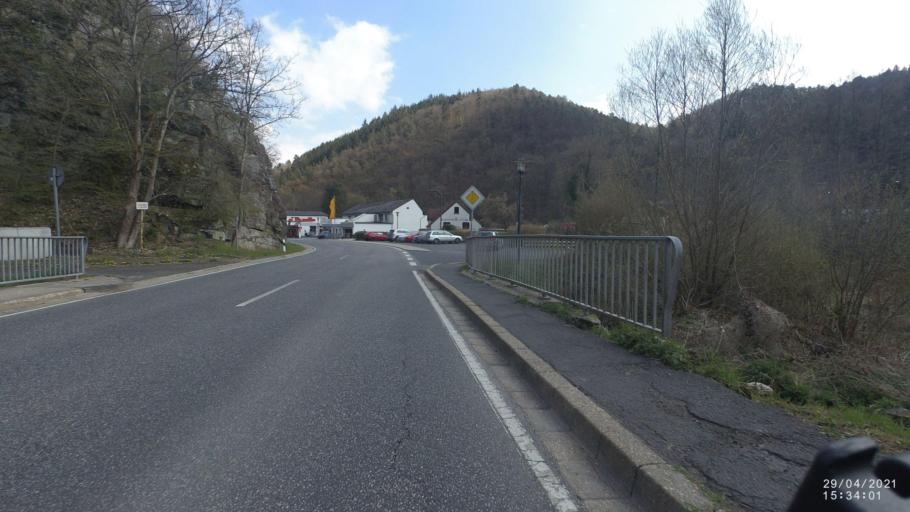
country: DE
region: Rheinland-Pfalz
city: Volkesfeld
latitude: 50.3839
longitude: 7.1524
